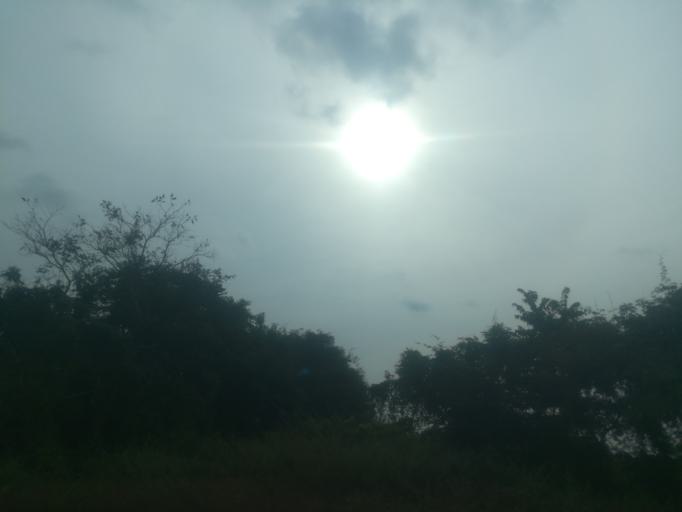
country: NG
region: Ogun
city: Ayetoro
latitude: 7.2922
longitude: 3.0792
